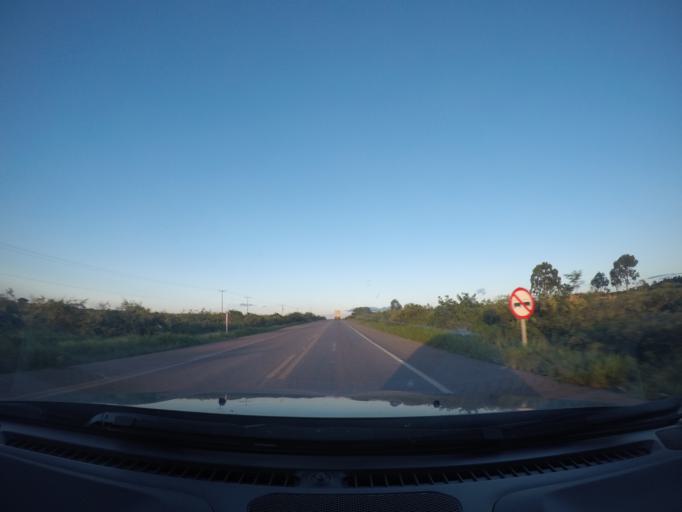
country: BR
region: Bahia
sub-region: Seabra
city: Seabra
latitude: -12.4179
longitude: -41.9831
